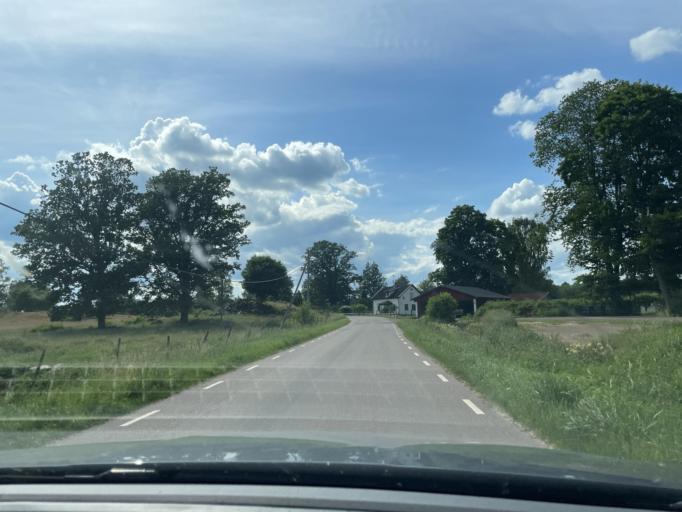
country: SE
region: Kalmar
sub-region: Vimmerby Kommun
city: Sodra Vi
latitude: 57.8161
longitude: 15.7590
